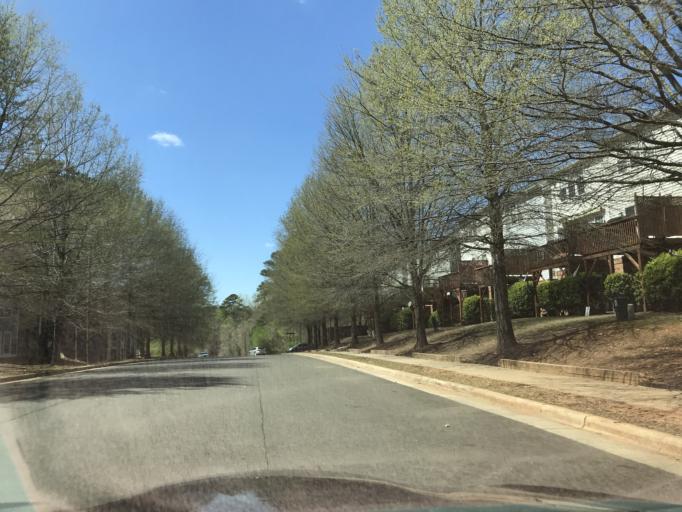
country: US
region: North Carolina
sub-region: Wake County
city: Cary
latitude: 35.8776
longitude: -78.7287
